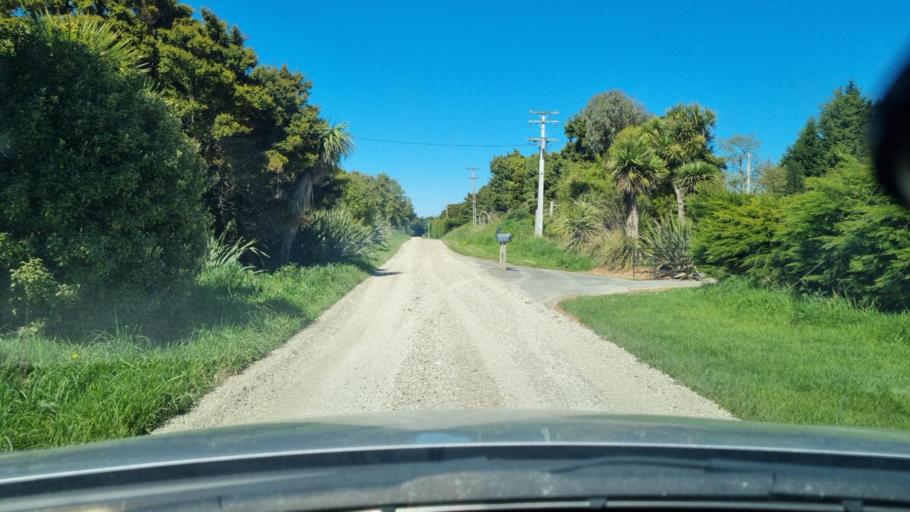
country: NZ
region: Southland
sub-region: Invercargill City
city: Invercargill
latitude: -46.4544
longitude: 168.2813
